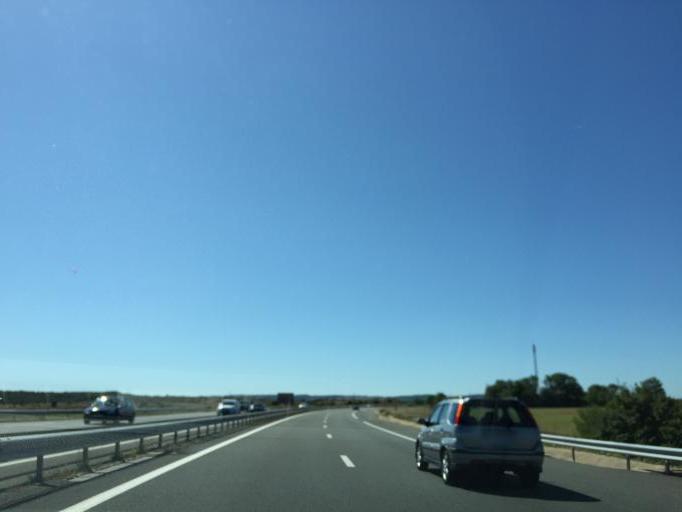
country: FR
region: Midi-Pyrenees
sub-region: Departement de l'Aveyron
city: La Cavalerie
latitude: 43.9676
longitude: 3.2095
